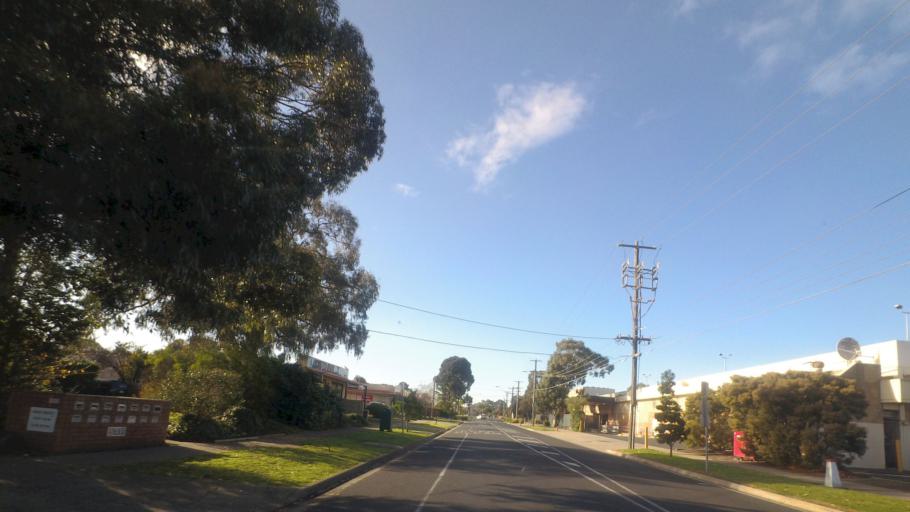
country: AU
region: Victoria
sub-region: Banyule
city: Bundoora
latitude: -37.6945
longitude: 145.0579
